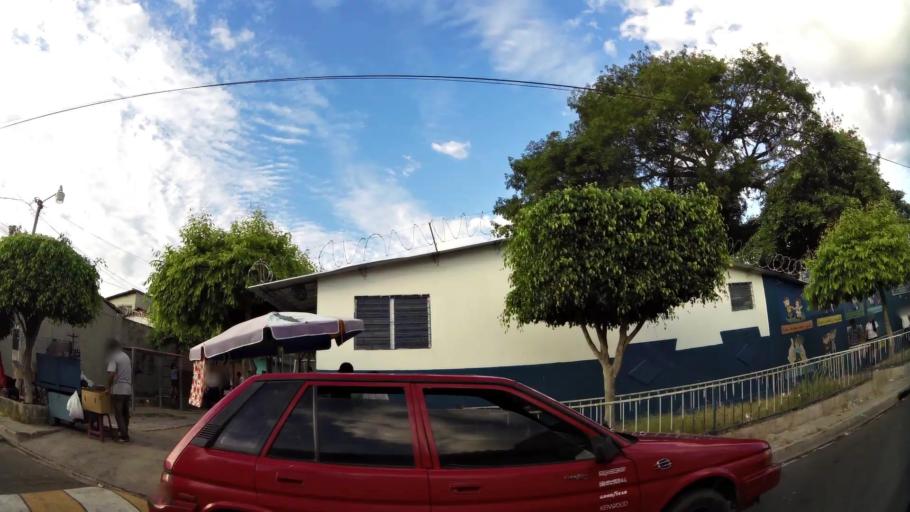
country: SV
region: Cuscatlan
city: Cojutepeque
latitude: 13.7214
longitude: -88.9297
